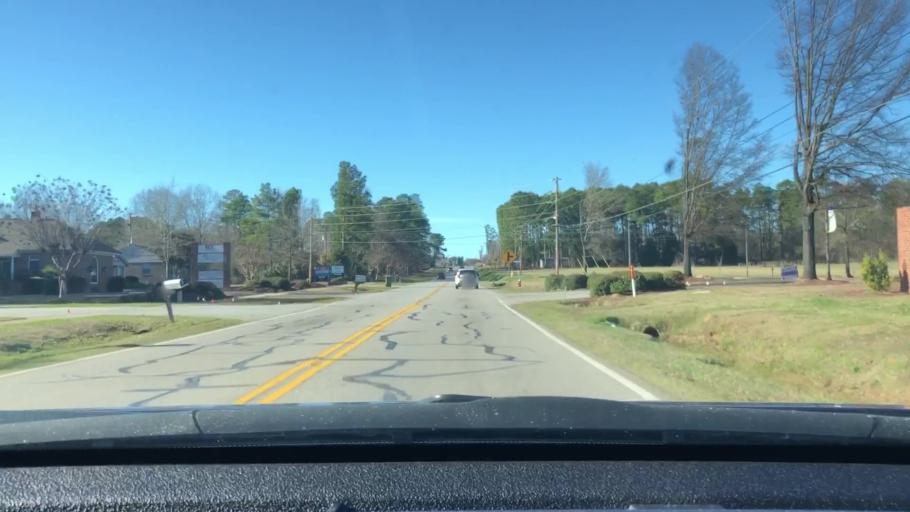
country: US
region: South Carolina
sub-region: Lexington County
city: Irmo
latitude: 34.1028
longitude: -81.1828
